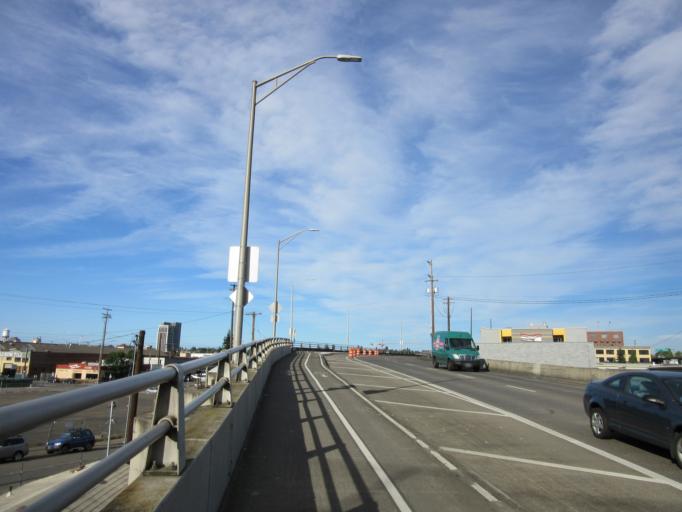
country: US
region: Oregon
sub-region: Multnomah County
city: Portland
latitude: 45.5126
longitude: -122.6670
